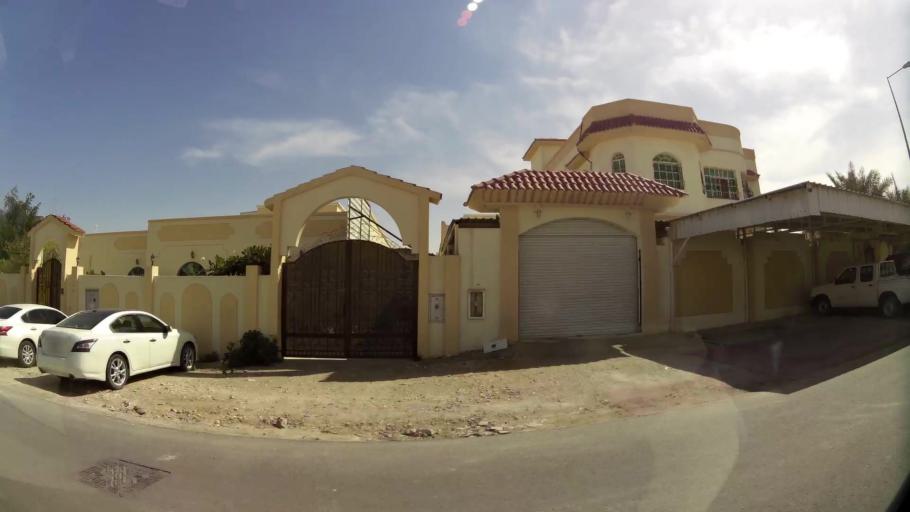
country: QA
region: Baladiyat ar Rayyan
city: Ar Rayyan
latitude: 25.2765
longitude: 51.4221
